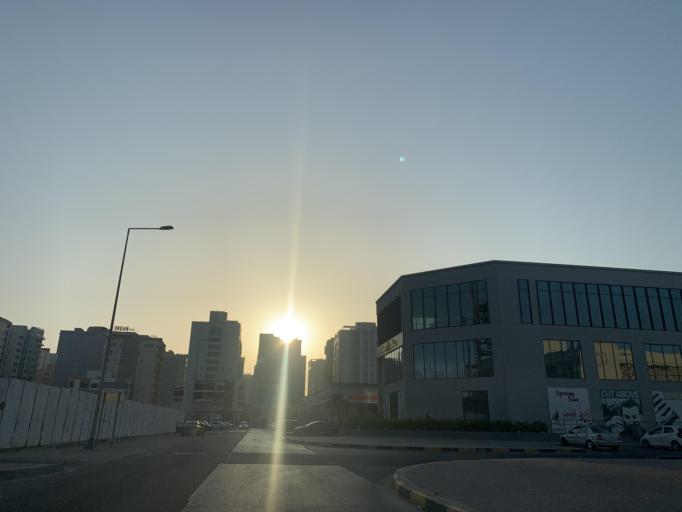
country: BH
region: Muharraq
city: Al Muharraq
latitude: 26.2650
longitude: 50.6002
